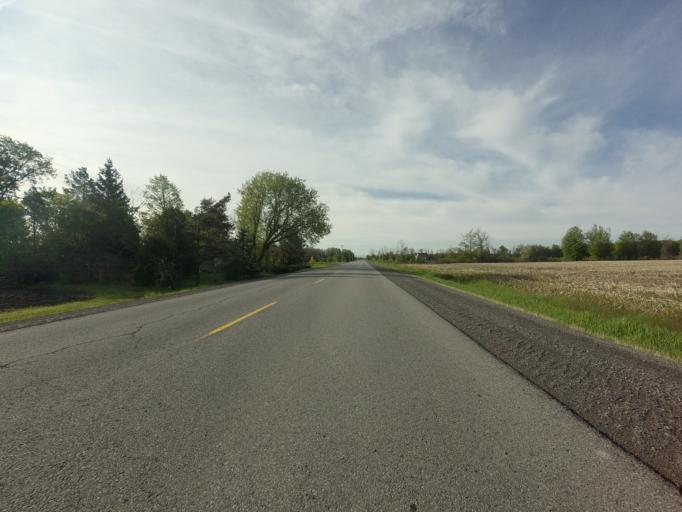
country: CA
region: Ontario
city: Ottawa
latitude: 45.2931
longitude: -75.4498
